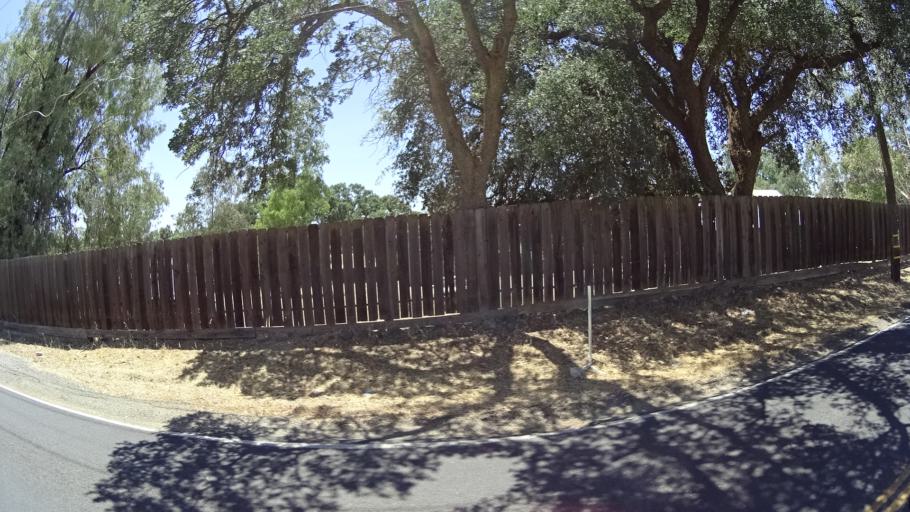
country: US
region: California
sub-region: Calaveras County
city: Rancho Calaveras
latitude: 38.0987
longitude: -120.8779
